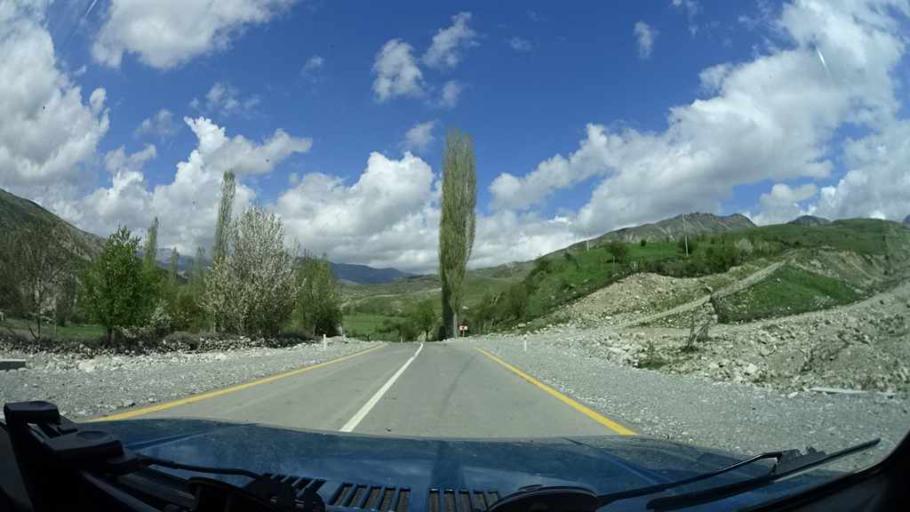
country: AZ
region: Ismayilli
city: Basqal
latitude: 40.8553
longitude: 48.3950
